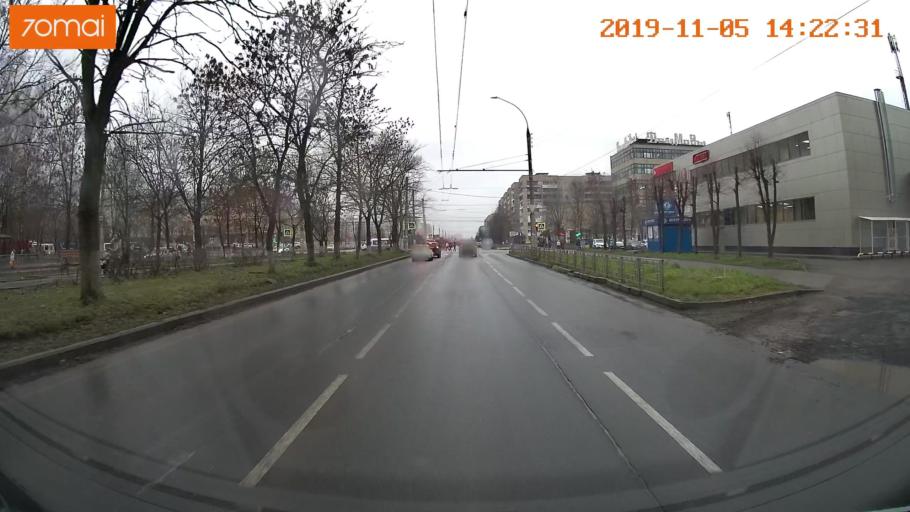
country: RU
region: Ivanovo
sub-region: Gorod Ivanovo
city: Ivanovo
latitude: 56.9642
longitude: 41.0035
